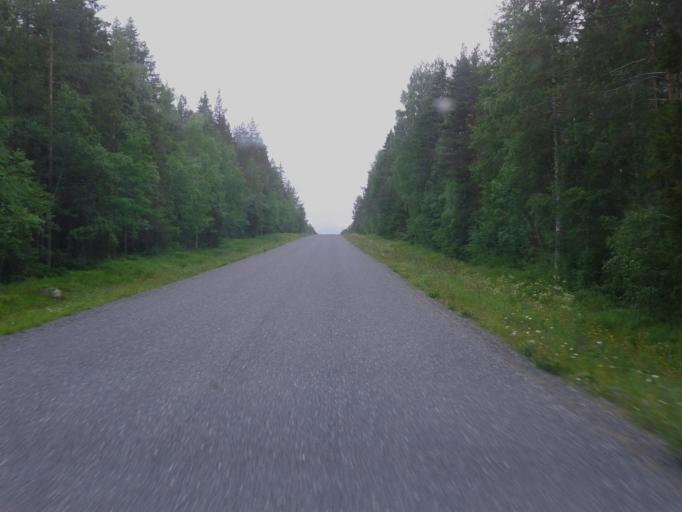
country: SE
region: Vaesterbotten
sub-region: Skelleftea Kommun
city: Storvik
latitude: 65.0028
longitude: 20.7424
